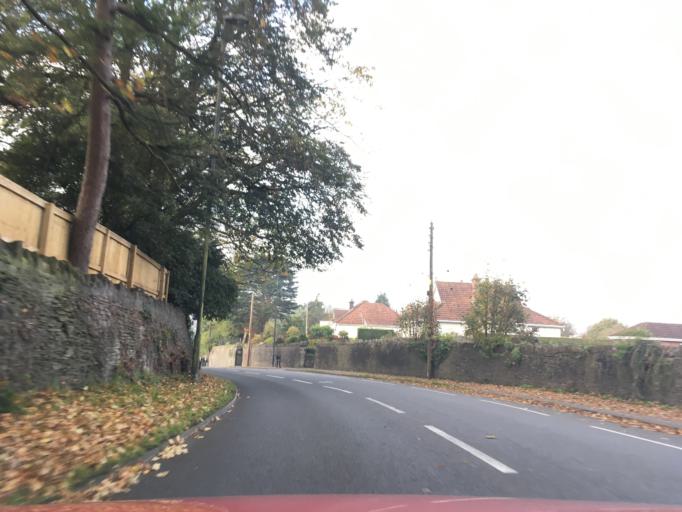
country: GB
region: England
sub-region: South Gloucestershire
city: Mangotsfield
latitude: 51.4823
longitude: -2.4883
